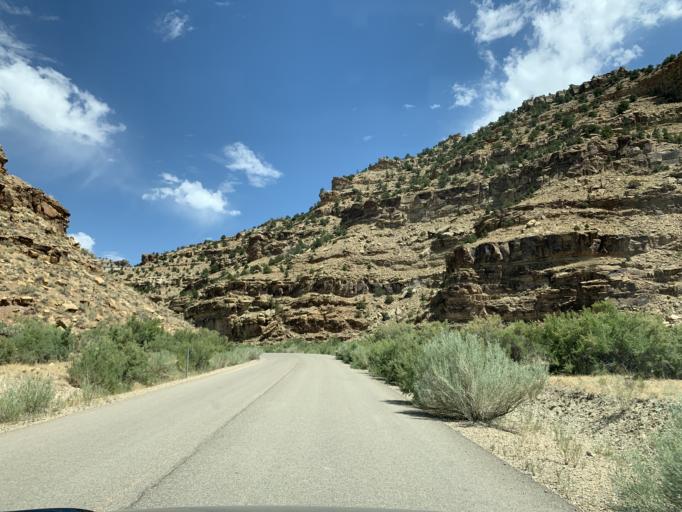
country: US
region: Utah
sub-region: Carbon County
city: East Carbon City
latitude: 39.8129
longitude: -110.2511
